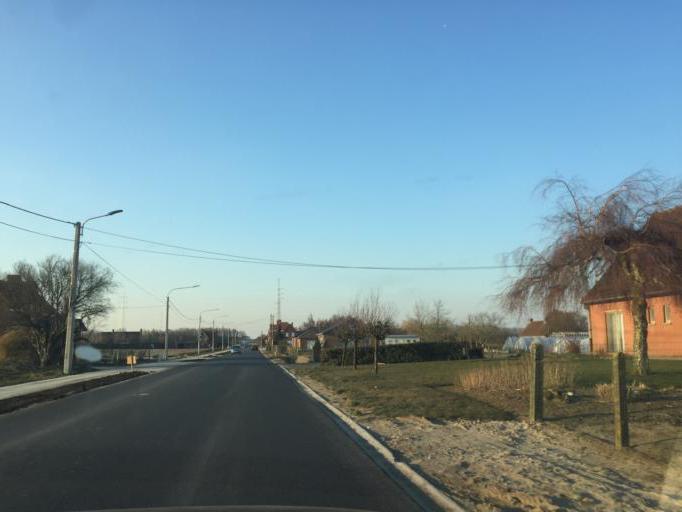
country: BE
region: Flanders
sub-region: Provincie West-Vlaanderen
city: Pittem
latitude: 50.9815
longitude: 3.2691
